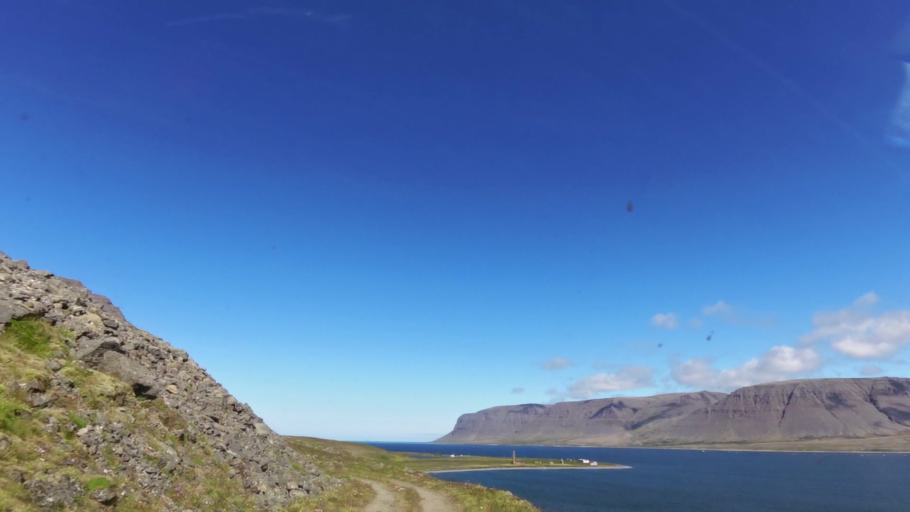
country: IS
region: West
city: Olafsvik
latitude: 65.6342
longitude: -23.9239
